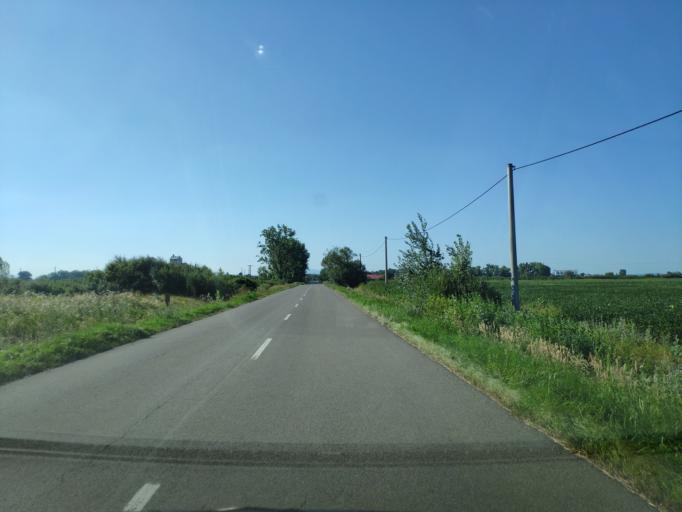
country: SK
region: Kosicky
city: Trebisov
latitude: 48.5677
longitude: 21.8628
